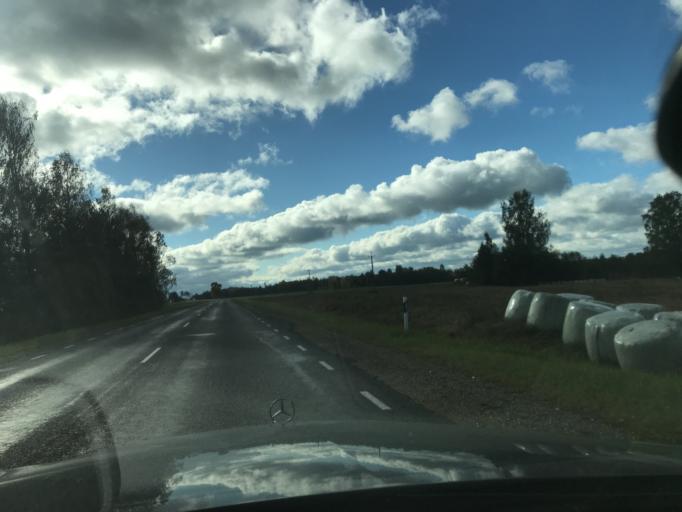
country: EE
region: Valgamaa
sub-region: Valga linn
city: Valga
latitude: 57.9775
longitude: 26.2607
